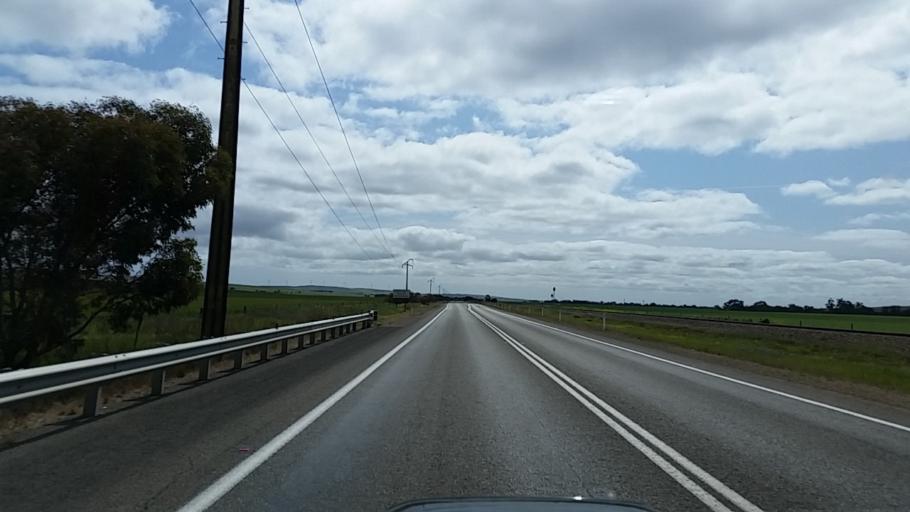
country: AU
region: South Australia
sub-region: Port Pirie City and Dists
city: Crystal Brook
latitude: -33.5331
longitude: 138.2107
